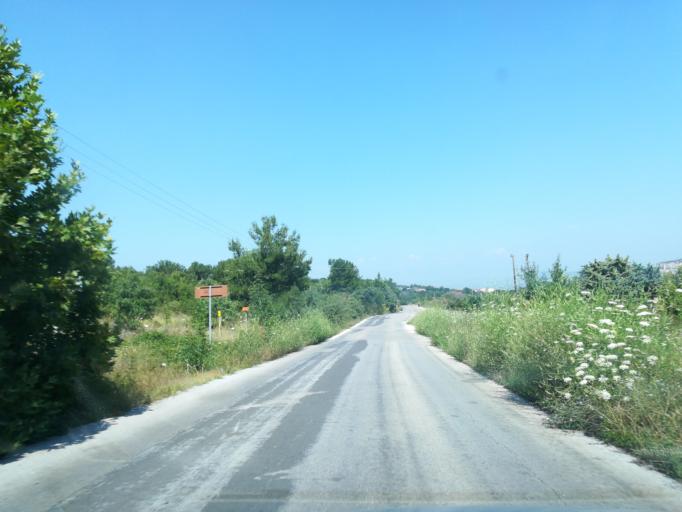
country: GR
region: Central Macedonia
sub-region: Nomos Thessalonikis
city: Asvestochori
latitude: 40.6300
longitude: 23.0327
